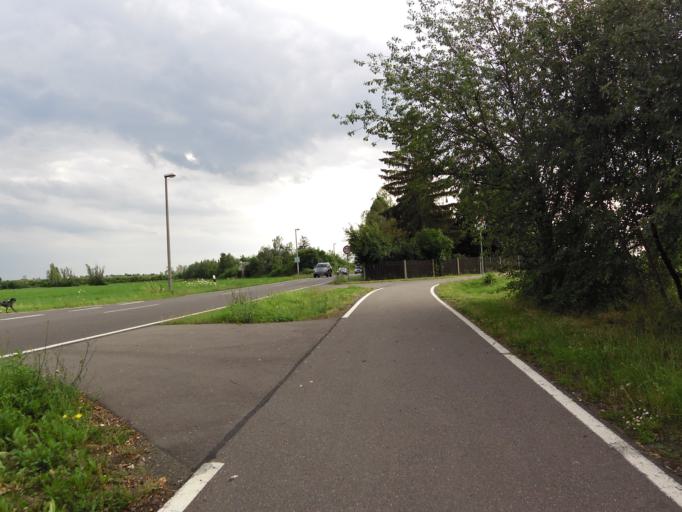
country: DE
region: Saxony
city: Zwenkau
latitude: 51.2635
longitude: 12.2925
